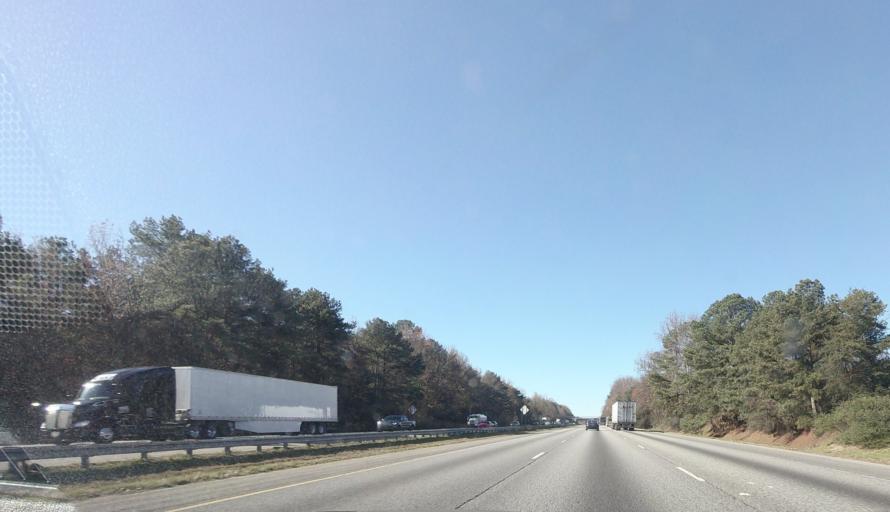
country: US
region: Georgia
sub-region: Douglas County
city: Lithia Springs
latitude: 33.7640
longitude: -84.6700
